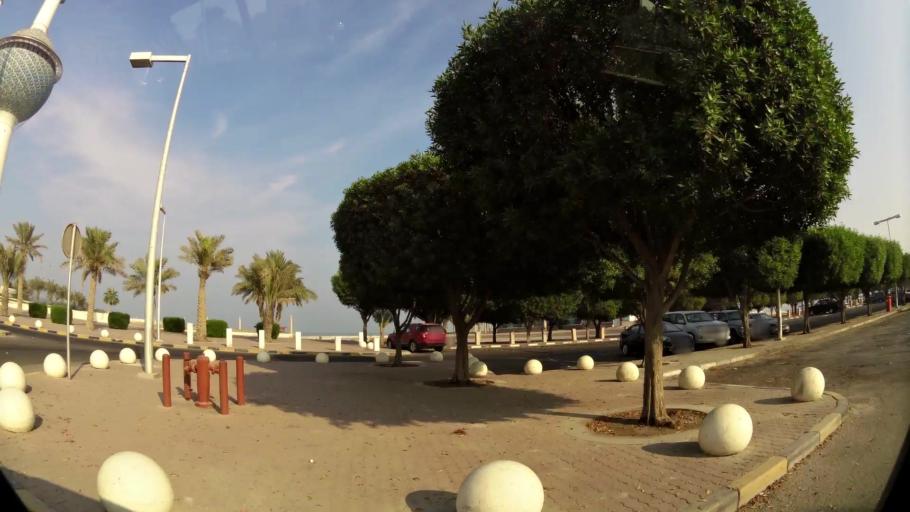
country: KW
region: Al Asimah
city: Ad Dasmah
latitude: 29.3888
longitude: 48.0023
